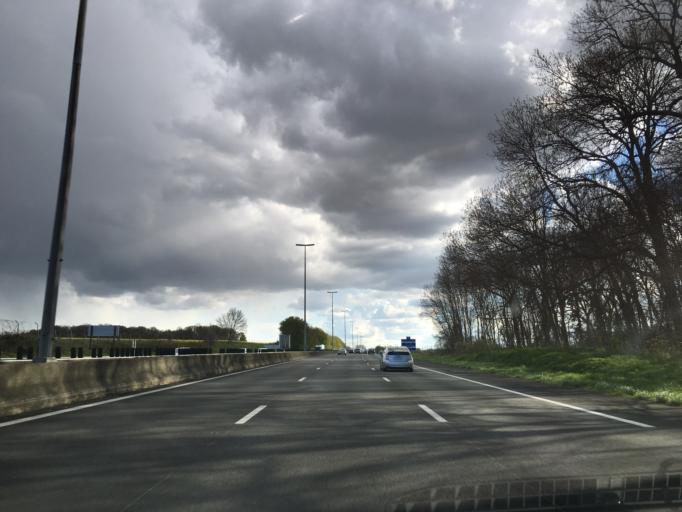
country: FR
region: Ile-de-France
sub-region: Departement du Val-d'Oise
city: Survilliers
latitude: 49.1173
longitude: 2.5555
